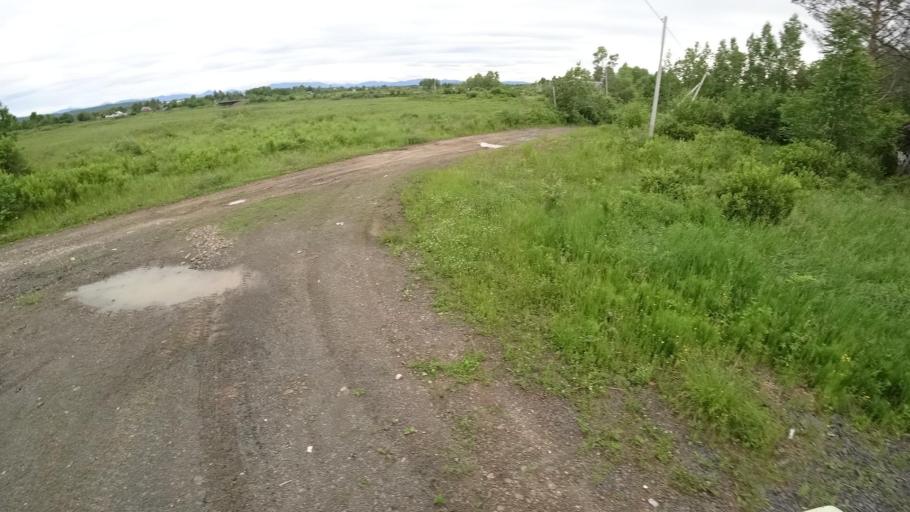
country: RU
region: Khabarovsk Krai
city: Amursk
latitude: 49.8946
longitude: 136.1458
